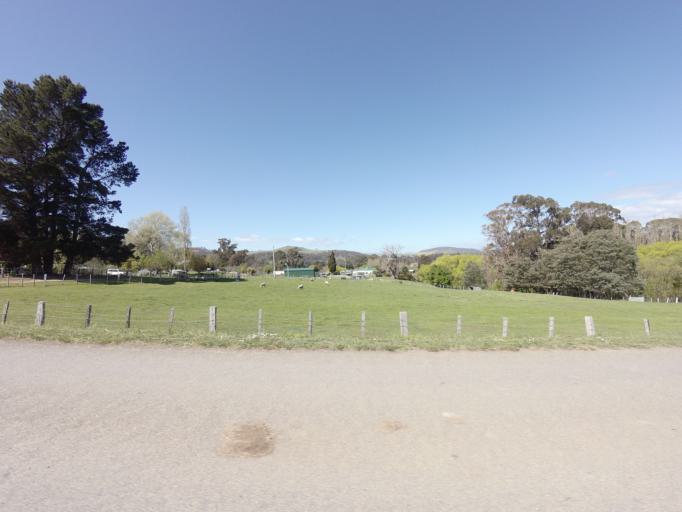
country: AU
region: Tasmania
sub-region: Derwent Valley
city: New Norfolk
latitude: -42.6702
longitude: 146.7902
